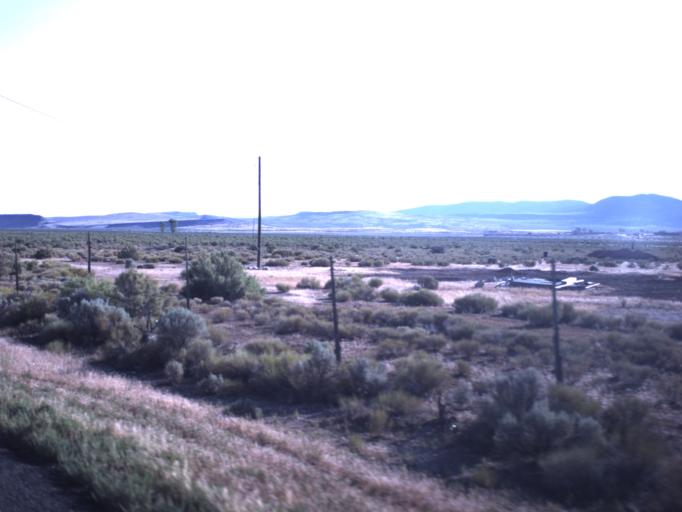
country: US
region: Utah
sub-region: Iron County
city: Enoch
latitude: 37.8031
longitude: -113.0505
